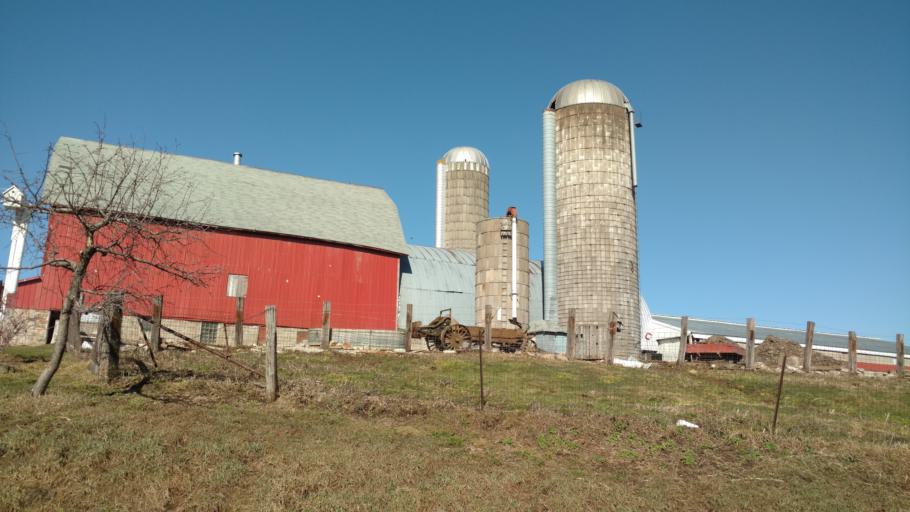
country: US
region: Wisconsin
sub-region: Vernon County
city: Hillsboro
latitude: 43.5921
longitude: -90.3785
